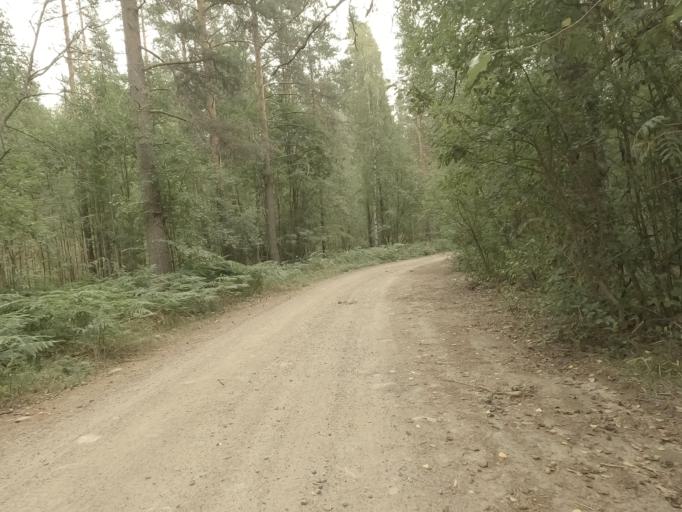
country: RU
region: Leningrad
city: Kamennogorsk
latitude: 60.9988
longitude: 29.1830
